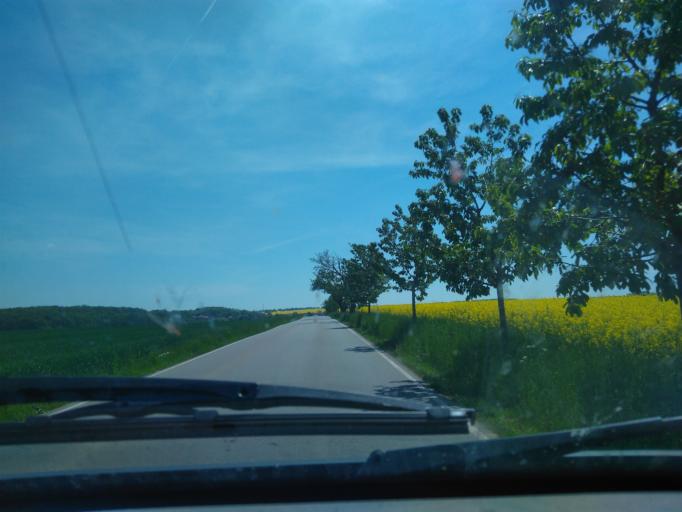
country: DE
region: Thuringia
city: Kromsdorf
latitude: 50.9937
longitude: 11.3806
